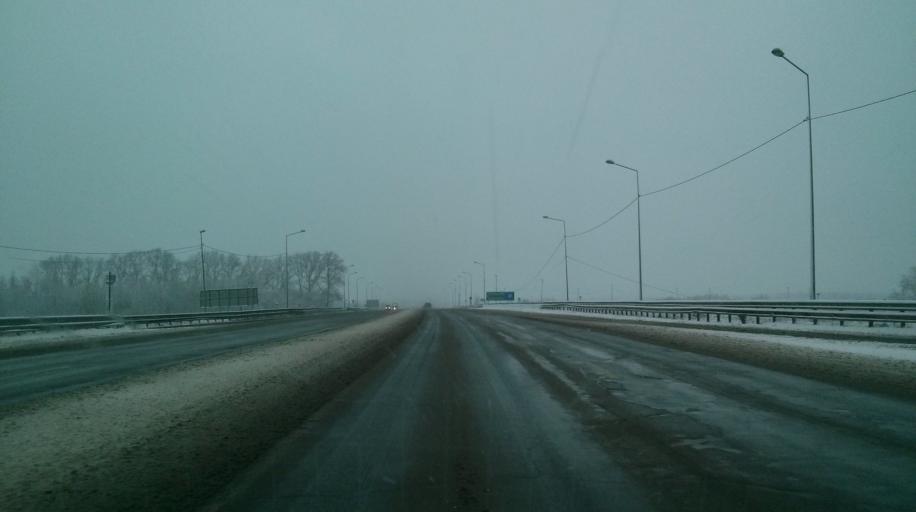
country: RU
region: Nizjnij Novgorod
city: Burevestnik
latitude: 56.1732
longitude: 43.7503
